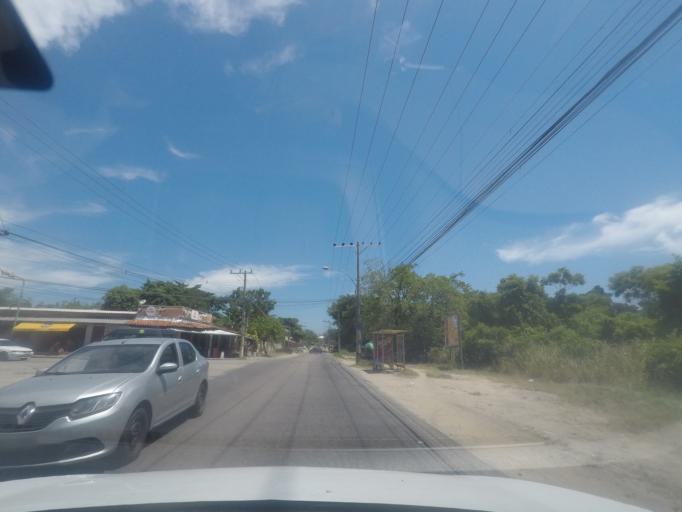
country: BR
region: Rio de Janeiro
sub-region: Itaguai
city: Itaguai
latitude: -22.9934
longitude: -43.6506
